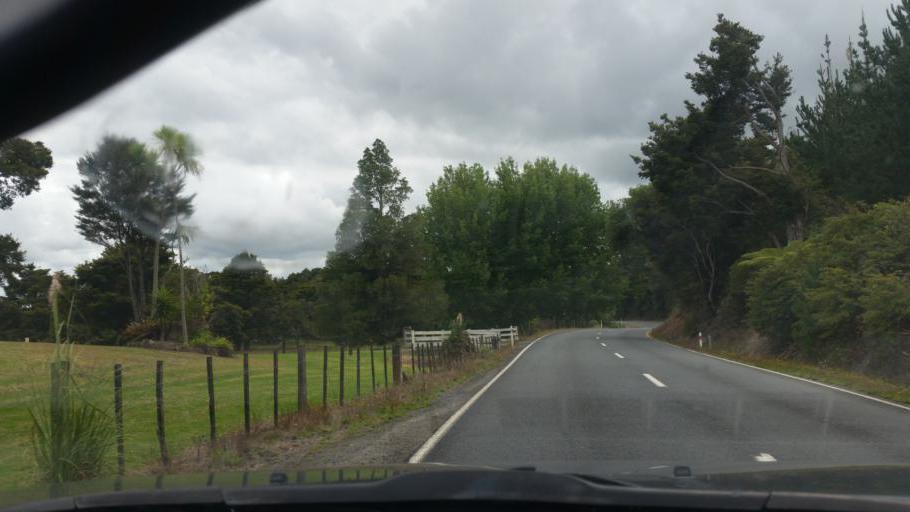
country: NZ
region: Northland
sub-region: Whangarei
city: Ruakaka
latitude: -35.9414
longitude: 174.2928
